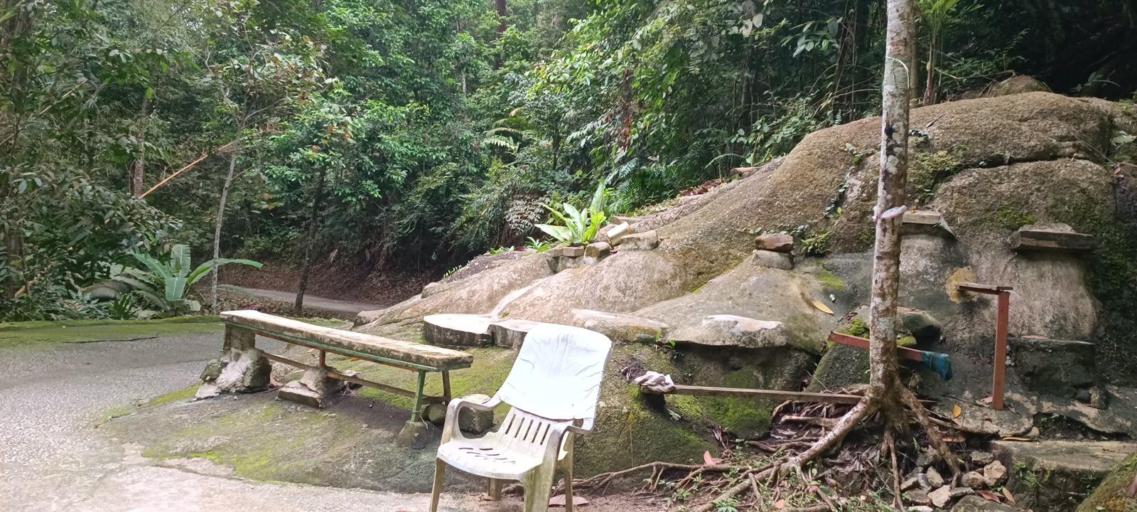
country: MY
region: Penang
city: Tanjung Tokong
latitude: 5.4034
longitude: 100.2629
